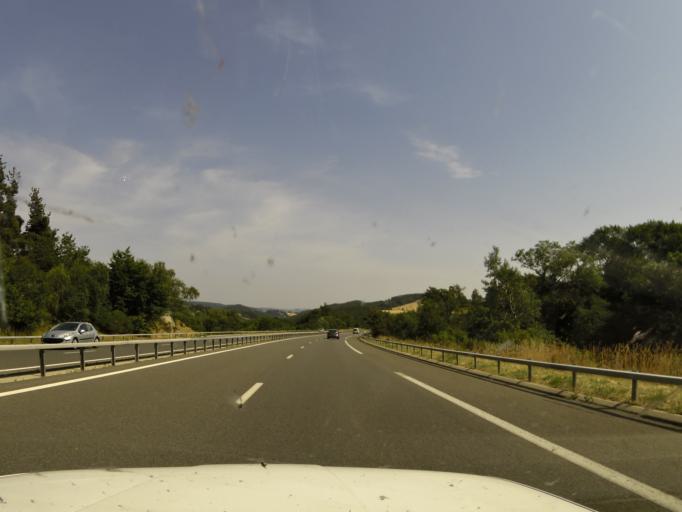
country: FR
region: Languedoc-Roussillon
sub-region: Departement de la Lozere
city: Marvejols
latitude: 44.6198
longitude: 3.2536
